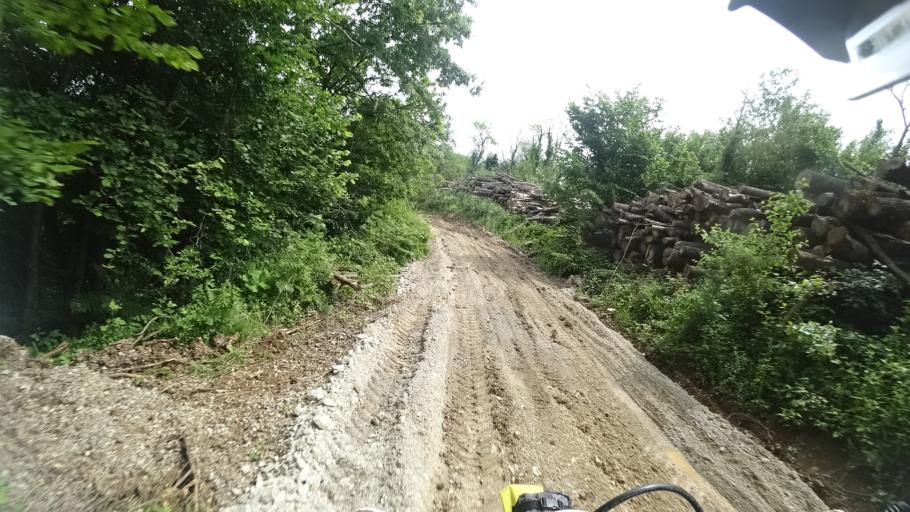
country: HR
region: Karlovacka
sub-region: Grad Karlovac
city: Slunj
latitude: 45.2001
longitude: 15.6261
